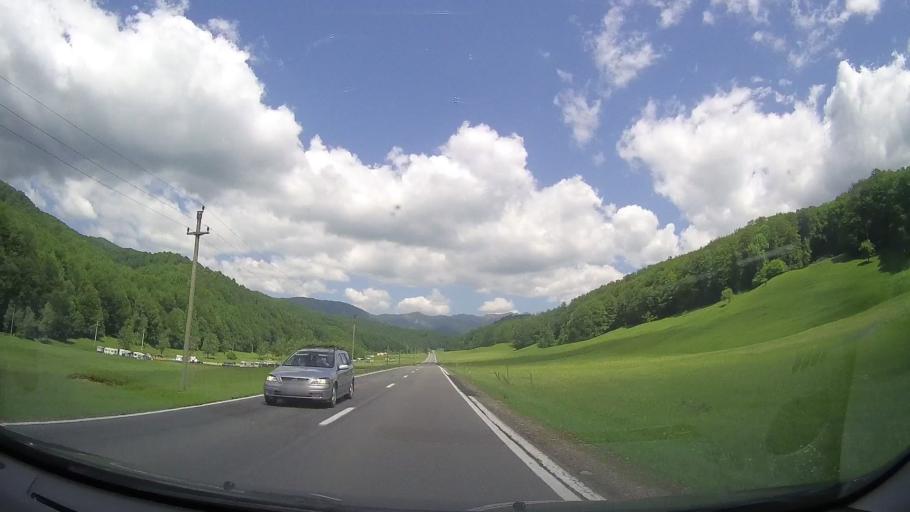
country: RO
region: Prahova
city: Maneciu
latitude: 45.4225
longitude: 25.9421
